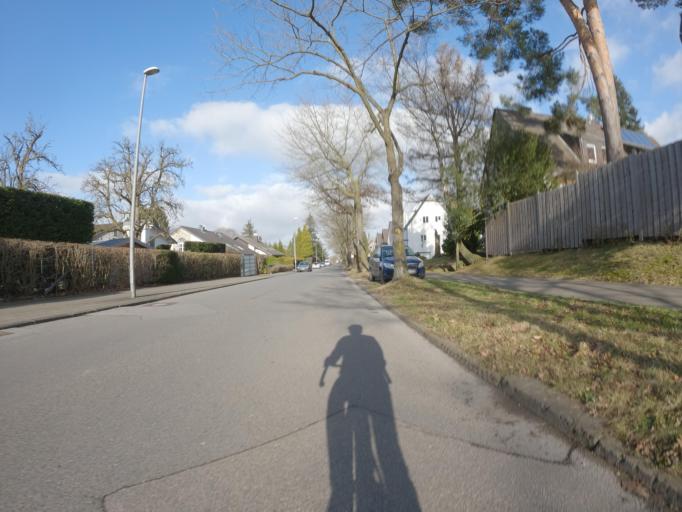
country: DE
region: North Rhine-Westphalia
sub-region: Regierungsbezirk Koln
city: Aachen
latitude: 50.7546
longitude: 6.1063
